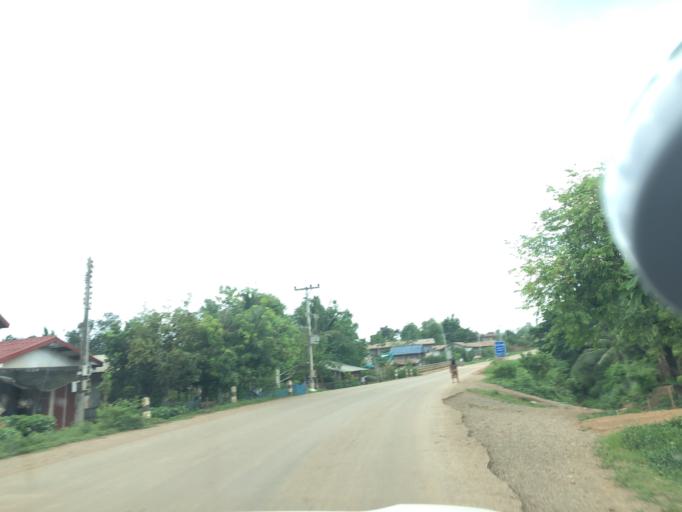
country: TH
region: Uttaradit
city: Ban Khok
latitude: 18.1122
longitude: 101.3728
